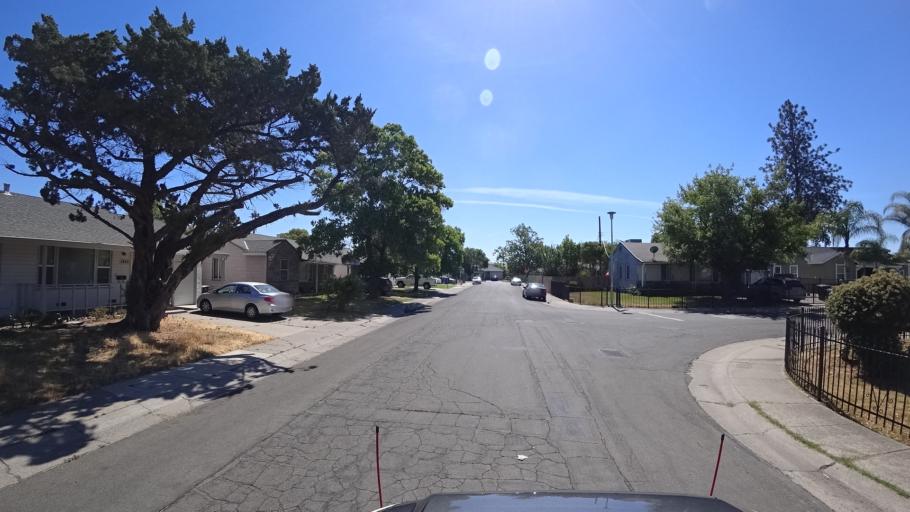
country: US
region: California
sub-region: Sacramento County
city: Parkway
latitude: 38.5185
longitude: -121.5019
